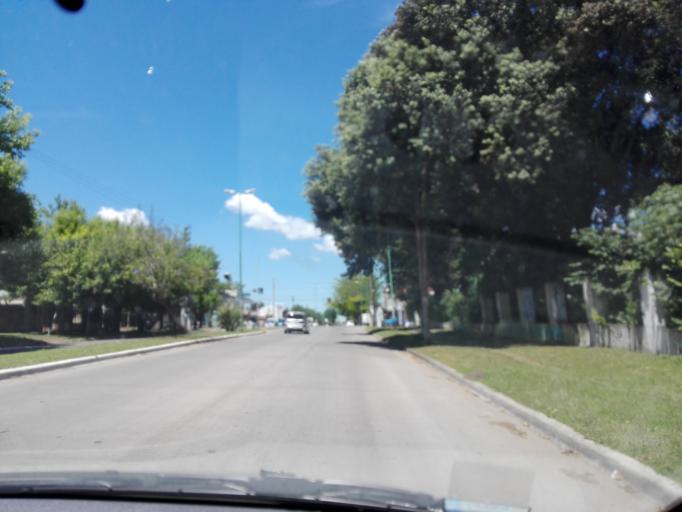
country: AR
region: Buenos Aires
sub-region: Partido de La Plata
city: La Plata
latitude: -34.8992
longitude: -58.0120
